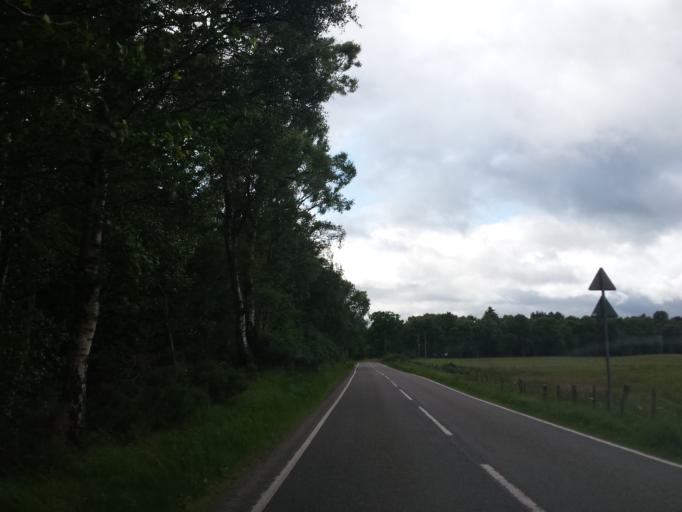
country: GB
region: Scotland
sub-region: Highland
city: Fortrose
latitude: 57.5109
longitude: -4.0197
